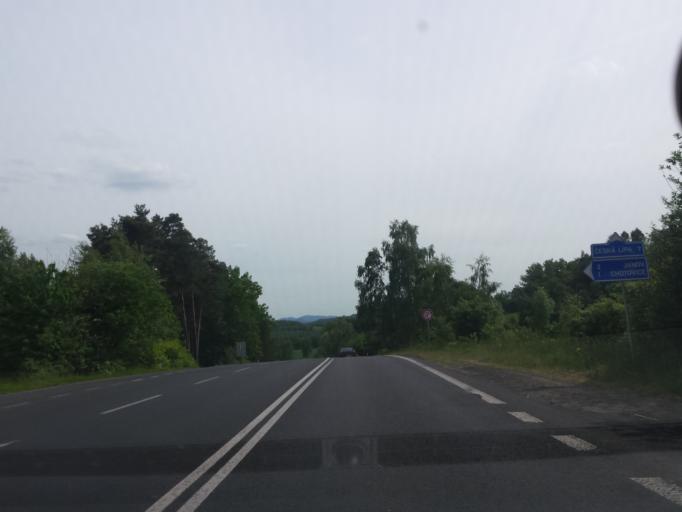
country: CZ
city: Novy Bor
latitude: 50.7431
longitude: 14.5511
